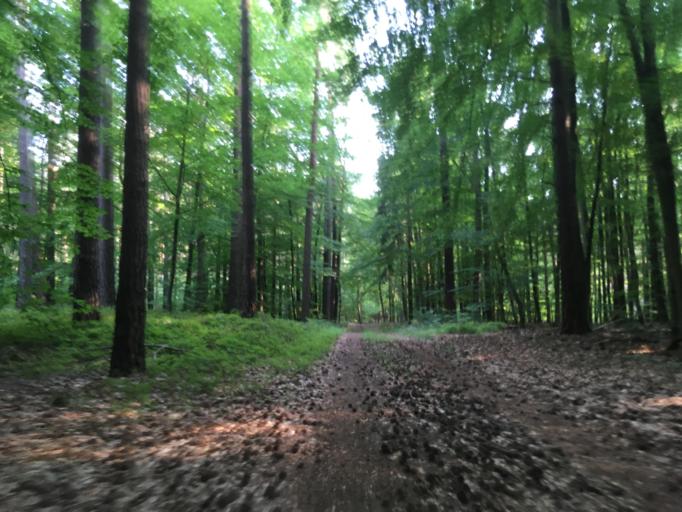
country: DE
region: Brandenburg
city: Wandlitz
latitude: 52.7276
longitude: 13.5285
